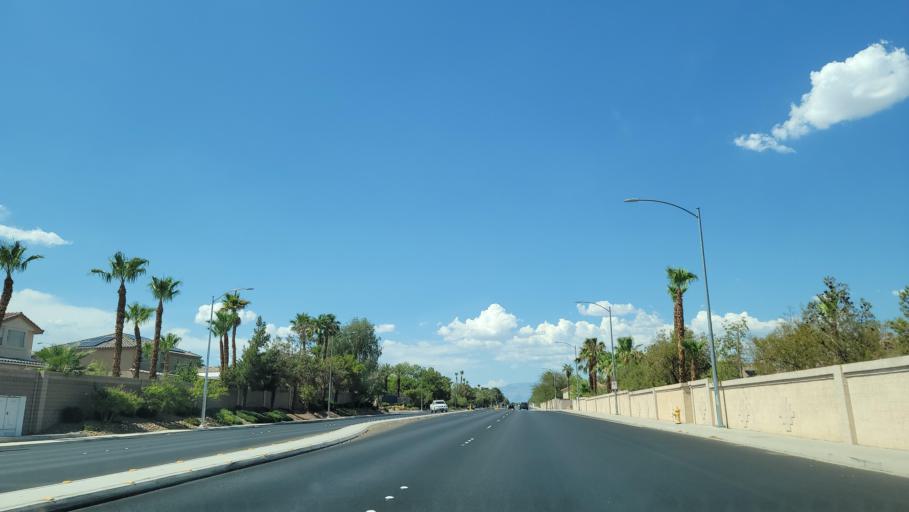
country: US
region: Nevada
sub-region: Clark County
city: Spring Valley
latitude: 36.1315
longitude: -115.2609
